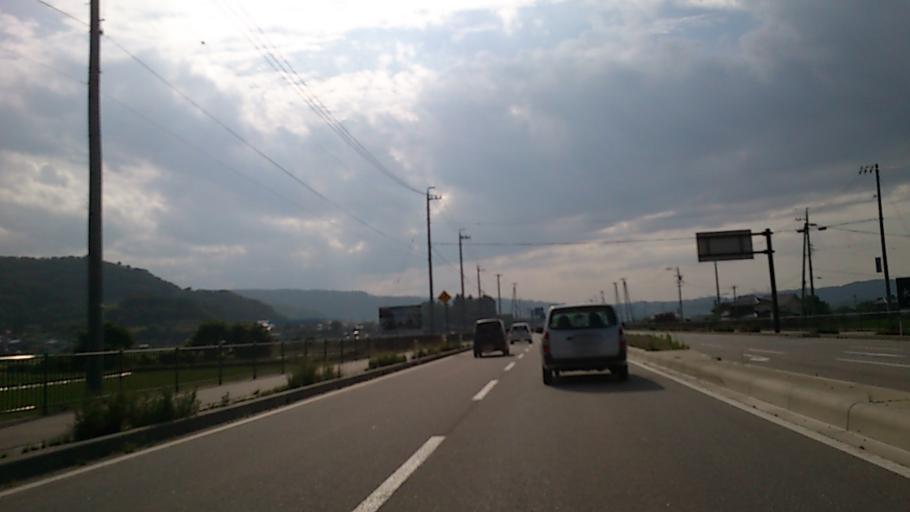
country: JP
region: Nagano
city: Saku
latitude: 36.2353
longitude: 138.4463
